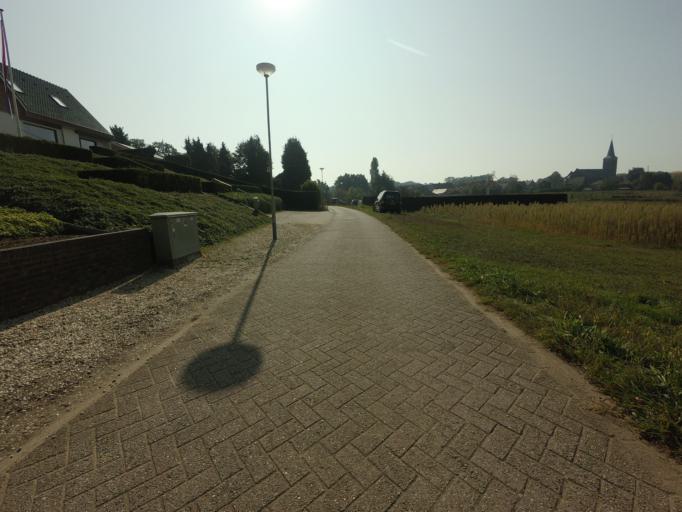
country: NL
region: Limburg
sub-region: Gemeente Beesel
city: Beesel
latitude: 51.2703
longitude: 6.0395
